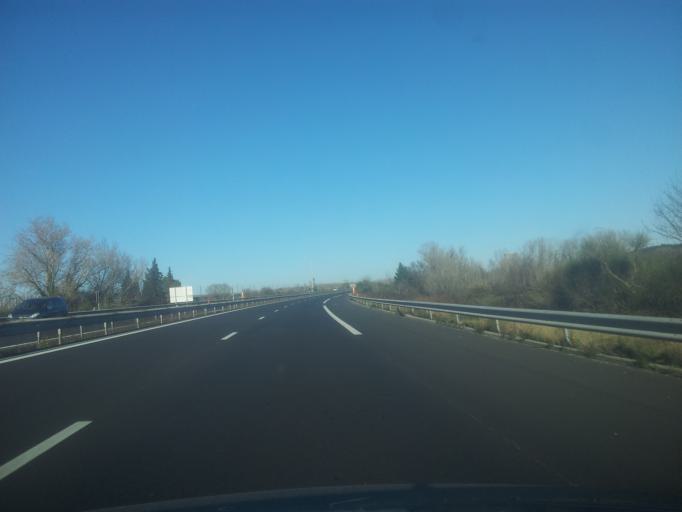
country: FR
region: Languedoc-Roussillon
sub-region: Departement du Gard
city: Montfaucon
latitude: 44.0653
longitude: 4.7653
